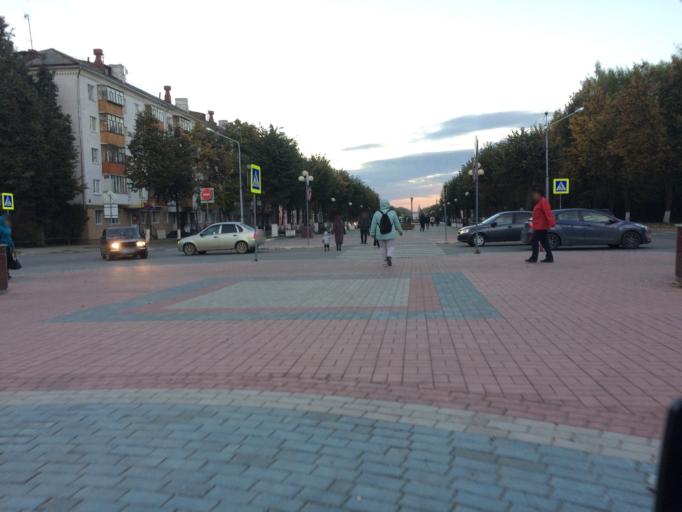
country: RU
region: Mariy-El
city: Yoshkar-Ola
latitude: 56.6392
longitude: 47.8768
